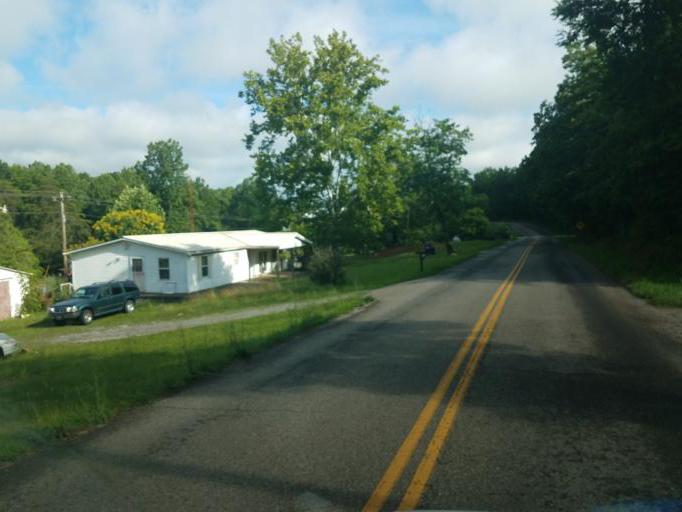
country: US
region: Ohio
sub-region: Gallia County
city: Gallipolis
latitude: 38.7784
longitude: -82.3872
